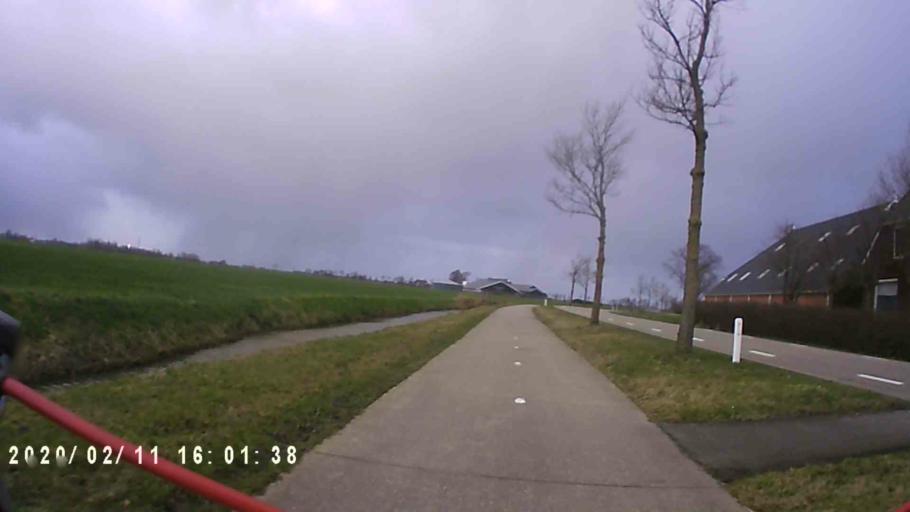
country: NL
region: Groningen
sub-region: Gemeente Zuidhorn
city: Oldehove
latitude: 53.2968
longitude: 6.4212
